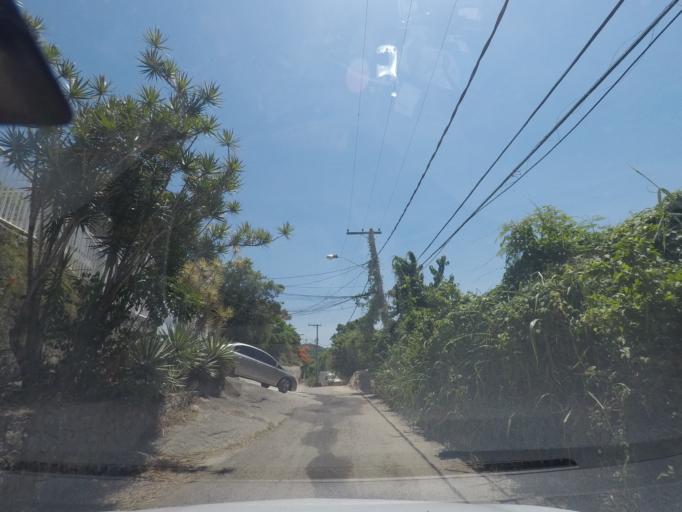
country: BR
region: Rio de Janeiro
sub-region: Niteroi
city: Niteroi
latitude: -22.9710
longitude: -43.0434
